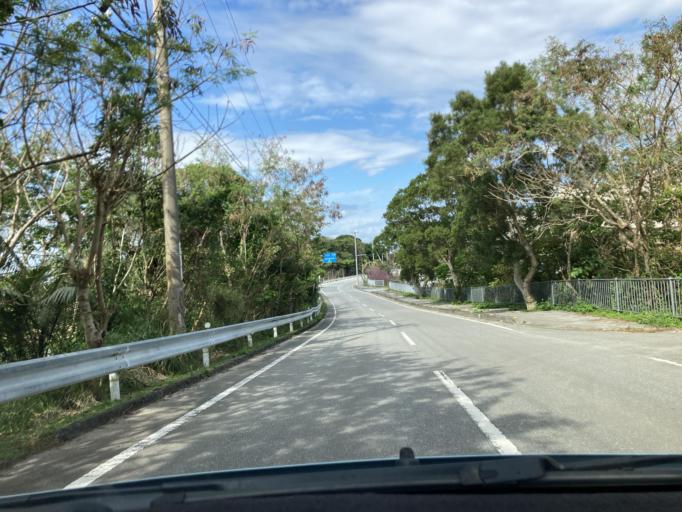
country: JP
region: Okinawa
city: Nago
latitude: 26.6982
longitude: 127.9247
